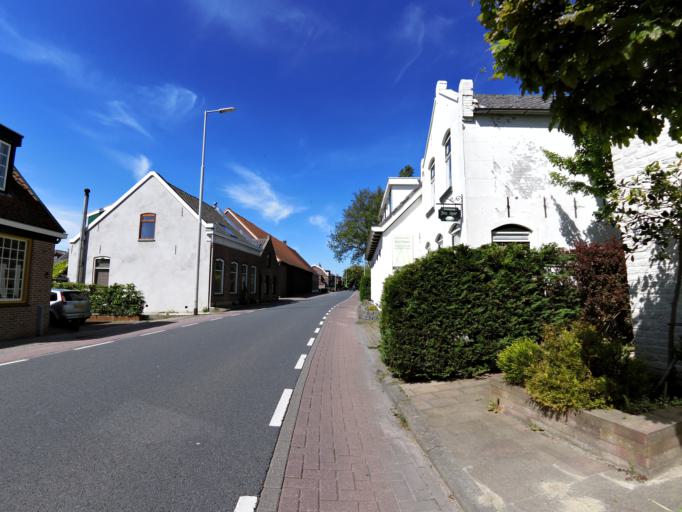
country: NL
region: South Holland
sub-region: Gemeente Hellevoetsluis
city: Nieuwenhoorn
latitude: 51.8514
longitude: 4.1386
